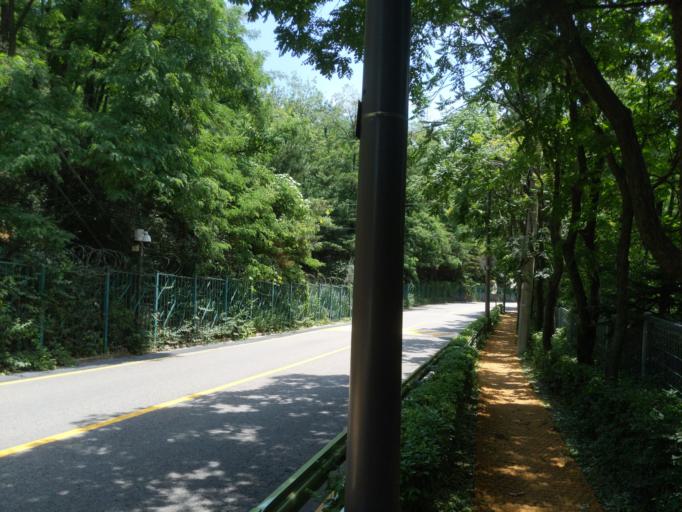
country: KR
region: Seoul
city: Seoul
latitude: 37.5984
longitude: 126.9737
